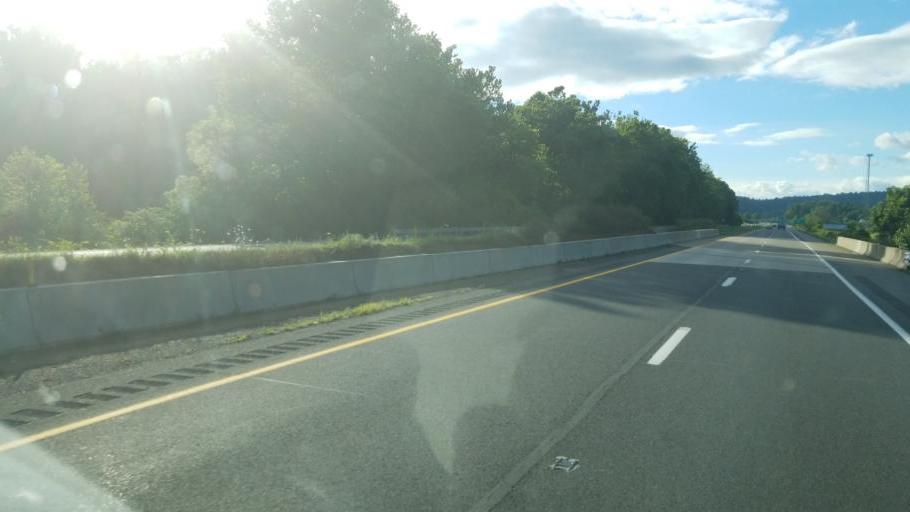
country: US
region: Maryland
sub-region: Washington County
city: Hancock
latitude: 39.7630
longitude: -78.1976
